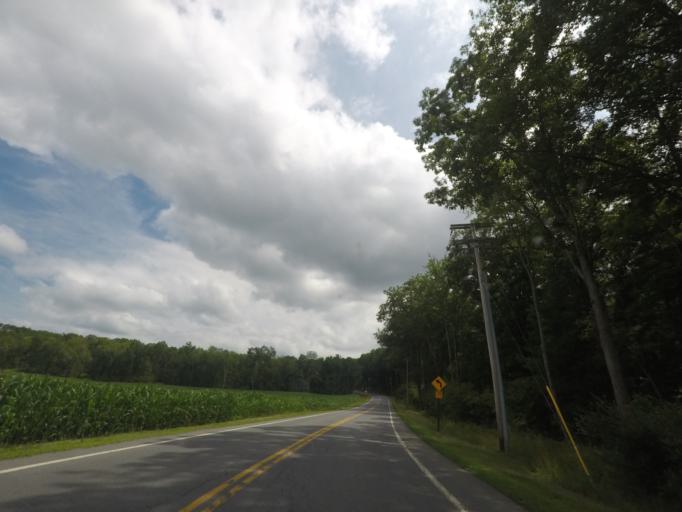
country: US
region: New York
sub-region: Saratoga County
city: Saratoga Springs
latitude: 43.0277
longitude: -73.7034
